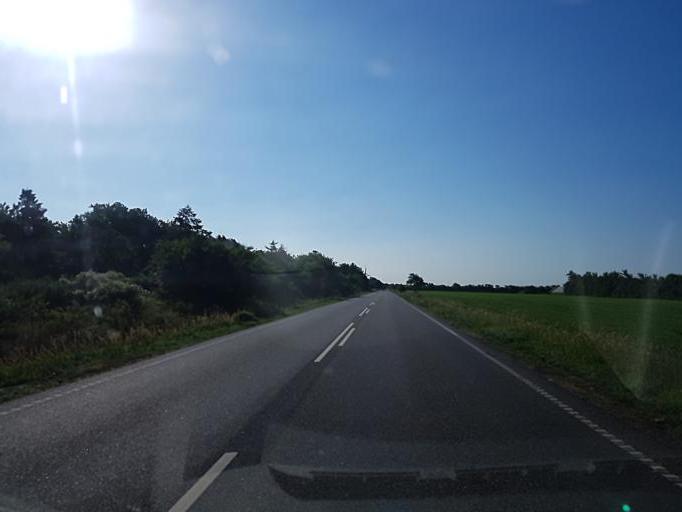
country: DK
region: Central Jutland
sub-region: Ringkobing-Skjern Kommune
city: Ringkobing
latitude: 56.1177
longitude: 8.2980
